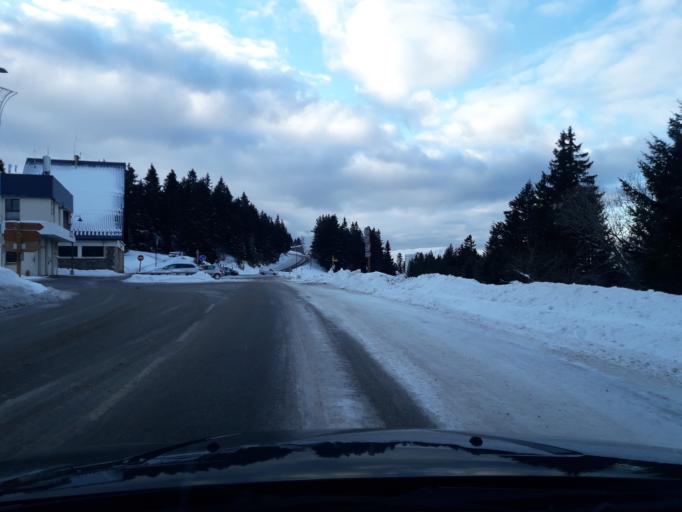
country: FR
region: Rhone-Alpes
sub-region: Departement de l'Isere
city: Vaulnaveys-le-Bas
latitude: 45.1121
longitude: 5.8746
